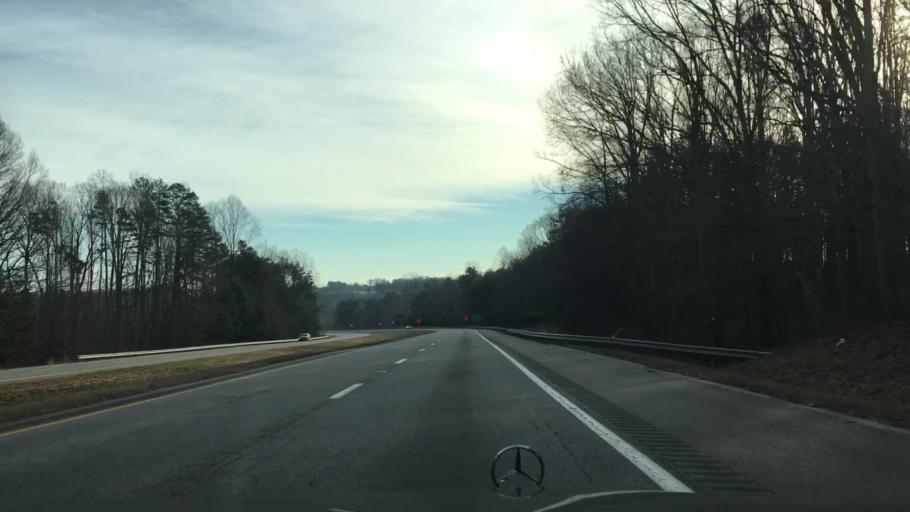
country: US
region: Virginia
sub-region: City of Danville
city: Danville
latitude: 36.5452
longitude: -79.4201
